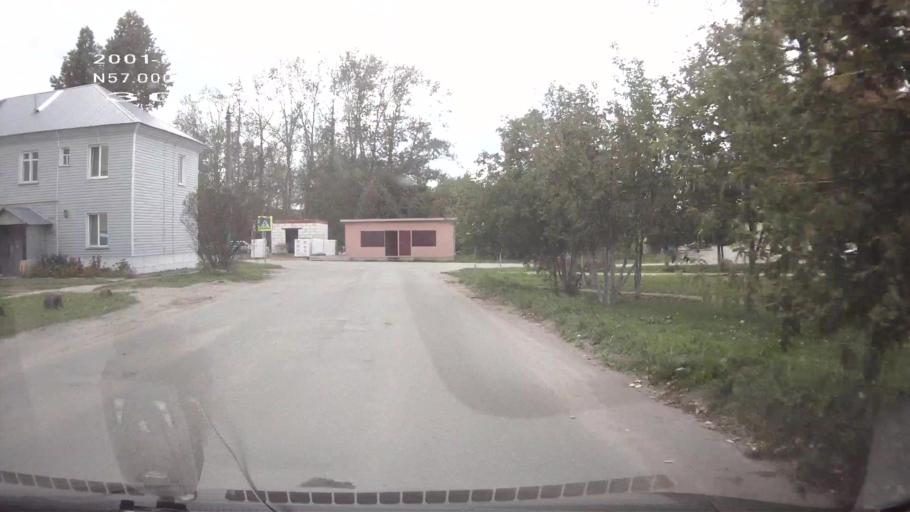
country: RU
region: Mariy-El
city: Kuzhener
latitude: 57.0008
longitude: 48.7391
